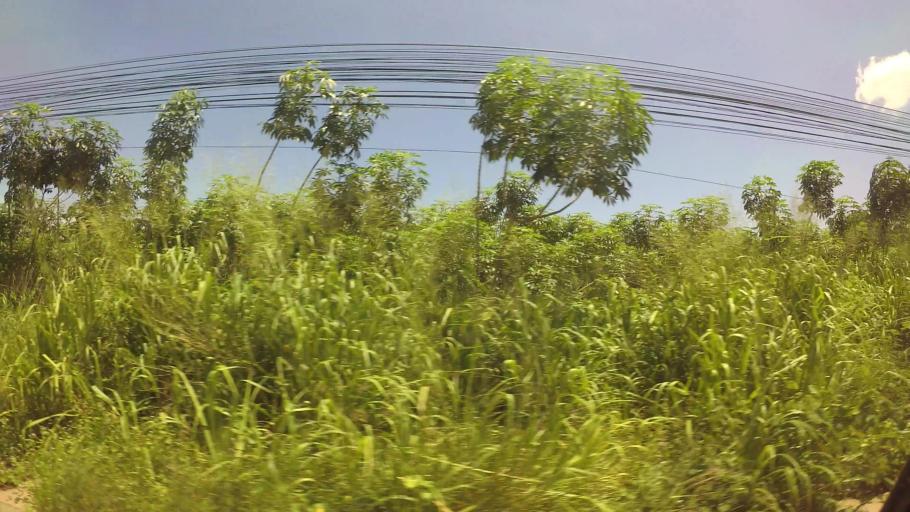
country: TH
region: Chon Buri
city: Si Racha
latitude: 13.1328
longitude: 100.9554
